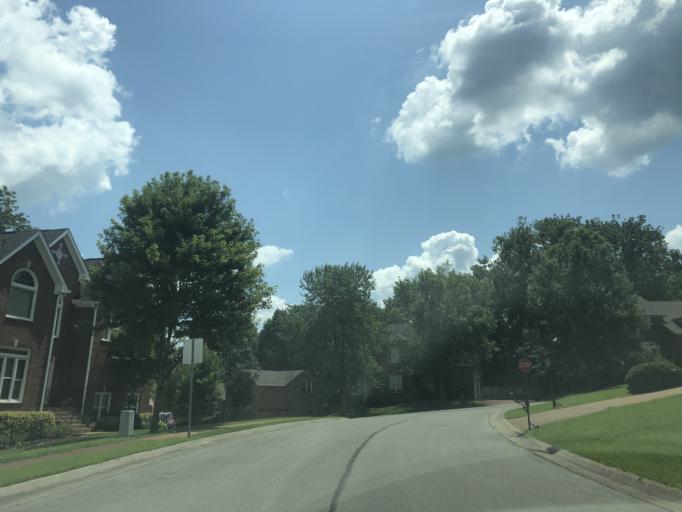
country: US
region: Tennessee
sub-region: Wilson County
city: Green Hill
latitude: 36.1531
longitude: -86.5920
